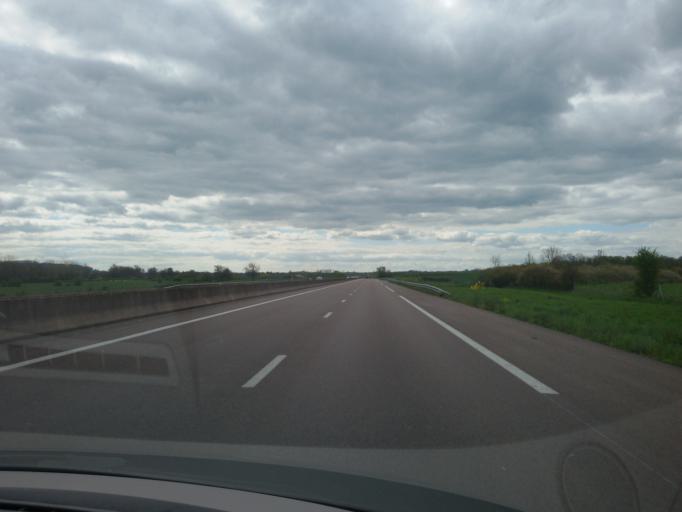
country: FR
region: Bourgogne
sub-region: Departement de la Cote-d'Or
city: Pouilly-en-Auxois
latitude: 47.2812
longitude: 4.5094
